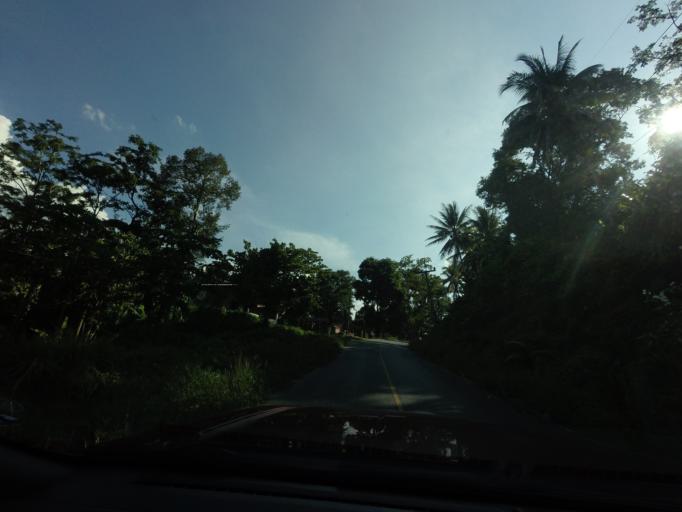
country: TH
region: Yala
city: Than To
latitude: 6.0875
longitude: 101.3257
